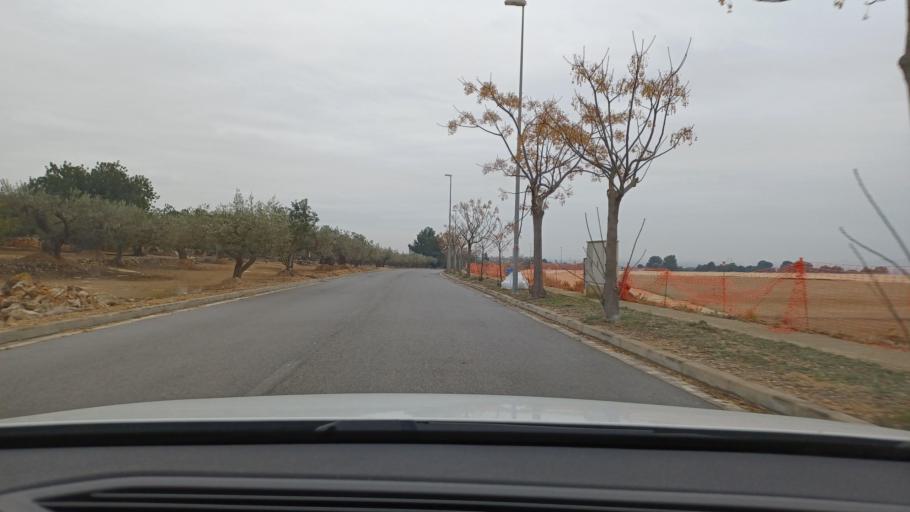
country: ES
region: Catalonia
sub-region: Provincia de Tarragona
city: Amposta
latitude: 40.7670
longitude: 0.5977
